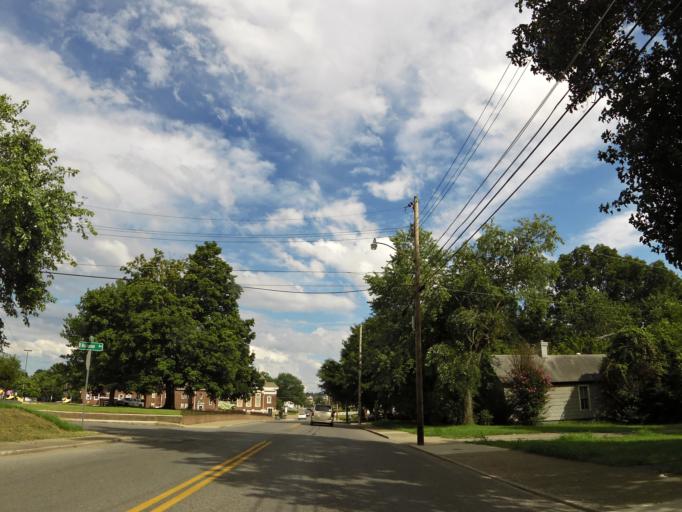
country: US
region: Kentucky
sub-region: Christian County
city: Hopkinsville
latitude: 36.8695
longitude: -87.4964
